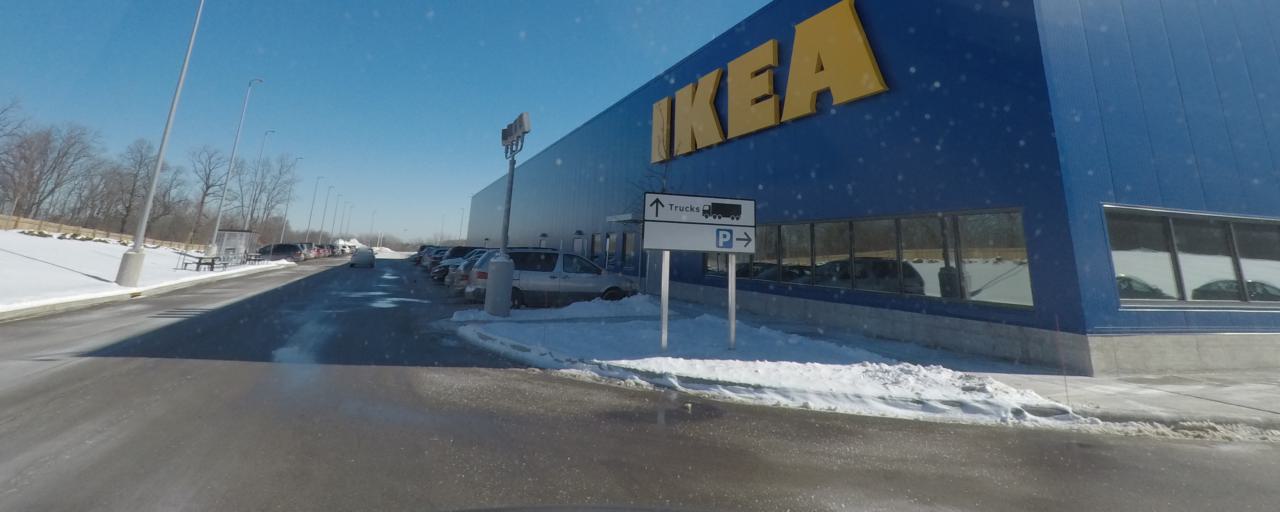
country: US
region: Wisconsin
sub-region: Milwaukee County
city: Greendale
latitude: 42.9085
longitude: -87.9399
